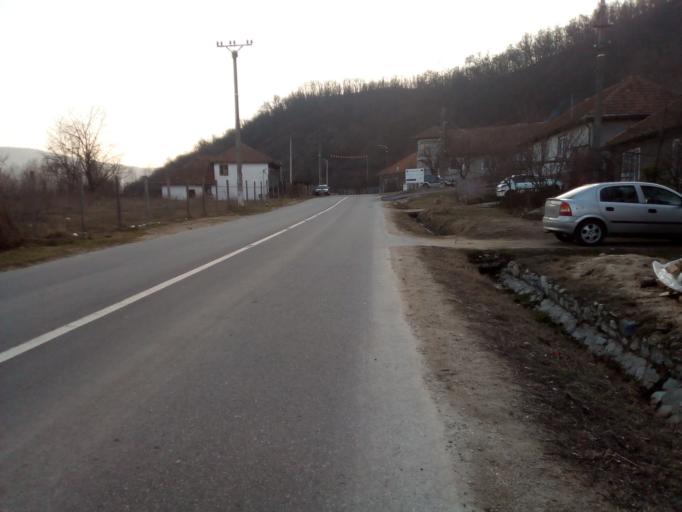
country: RO
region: Mehedinti
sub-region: Comuna Eselnita
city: Eselnita
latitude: 44.6917
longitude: 22.3646
